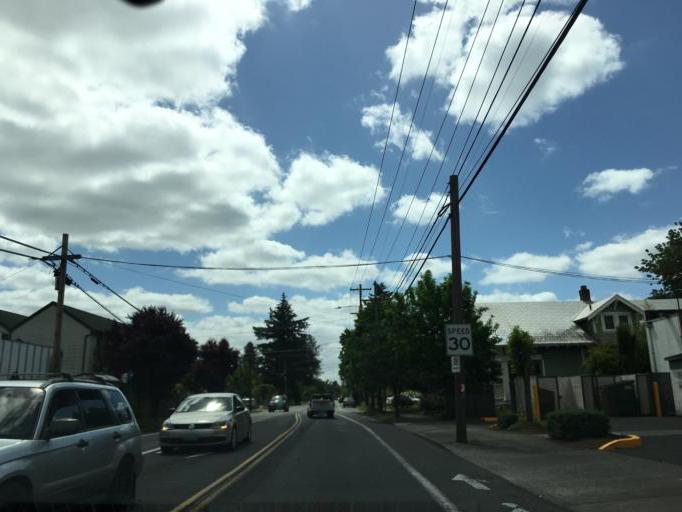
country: US
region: Oregon
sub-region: Multnomah County
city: Lents
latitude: 45.4904
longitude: -122.6090
